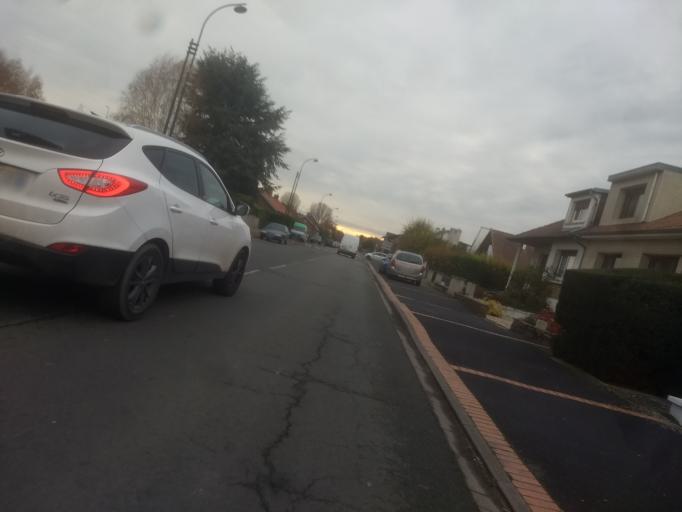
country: FR
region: Nord-Pas-de-Calais
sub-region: Departement du Pas-de-Calais
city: Dainville
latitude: 50.2855
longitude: 2.7403
